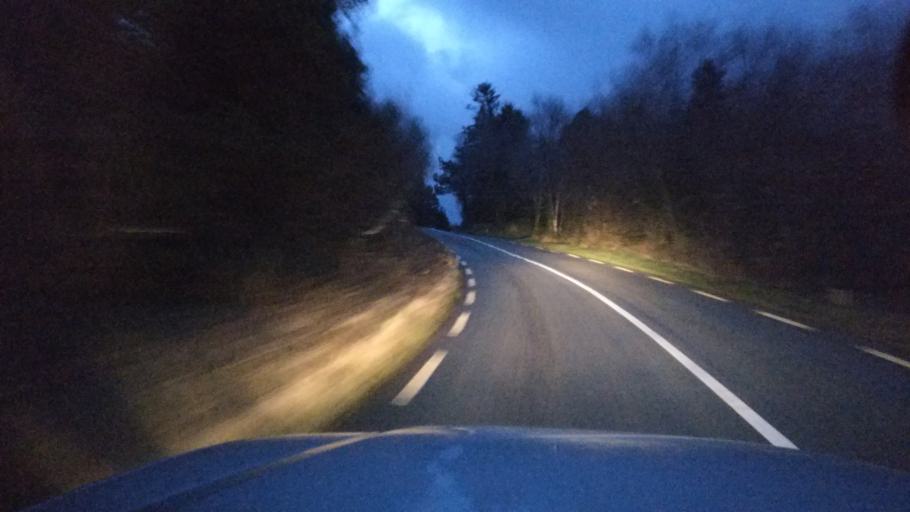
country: IE
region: Connaught
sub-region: County Galway
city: Oughterard
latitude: 53.3880
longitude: -9.5499
